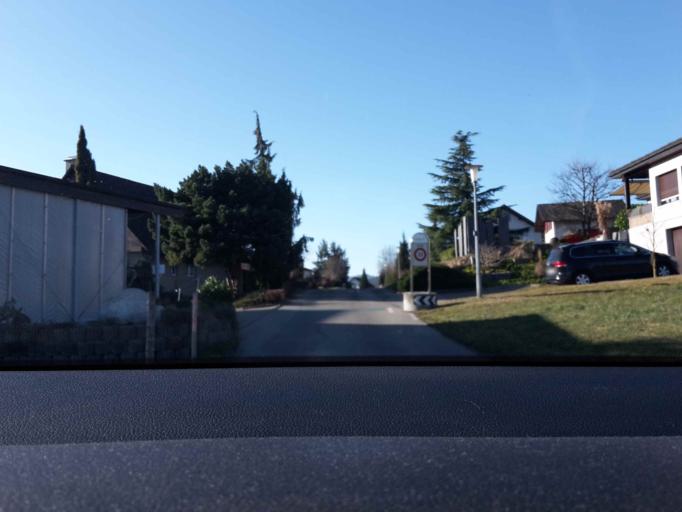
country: CH
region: Bern
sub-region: Oberaargau
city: Huttwil
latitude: 47.1177
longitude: 7.8633
